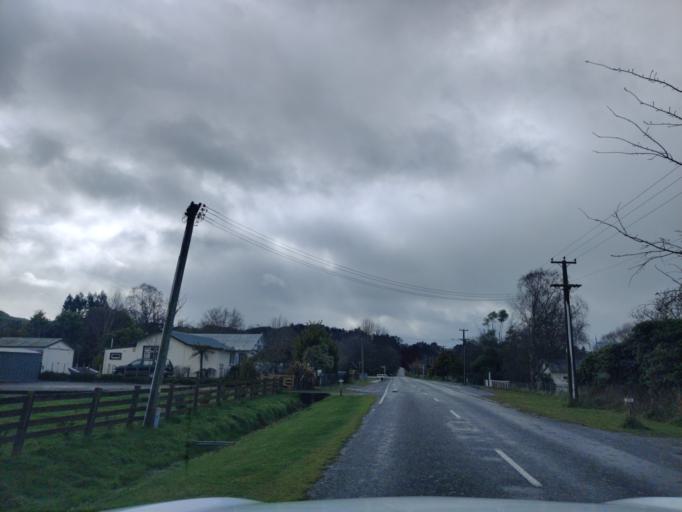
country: NZ
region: Manawatu-Wanganui
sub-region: Palmerston North City
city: Palmerston North
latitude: -40.1744
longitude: 175.7938
